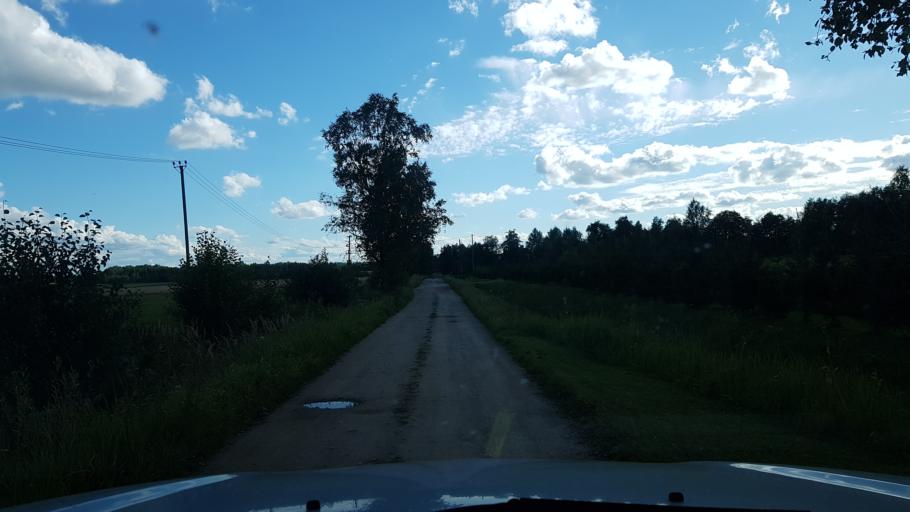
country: EE
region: Harju
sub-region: Rae vald
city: Jueri
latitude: 59.3618
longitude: 24.8579
